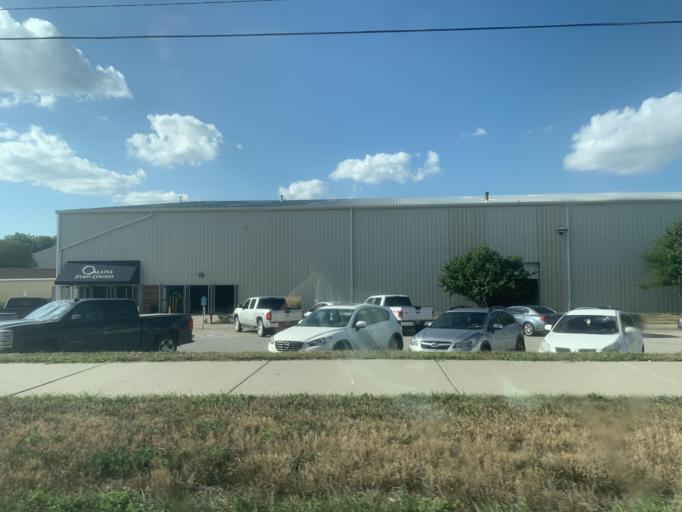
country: US
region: Nebraska
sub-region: Sarpy County
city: Chalco
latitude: 41.1764
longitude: -96.1450
